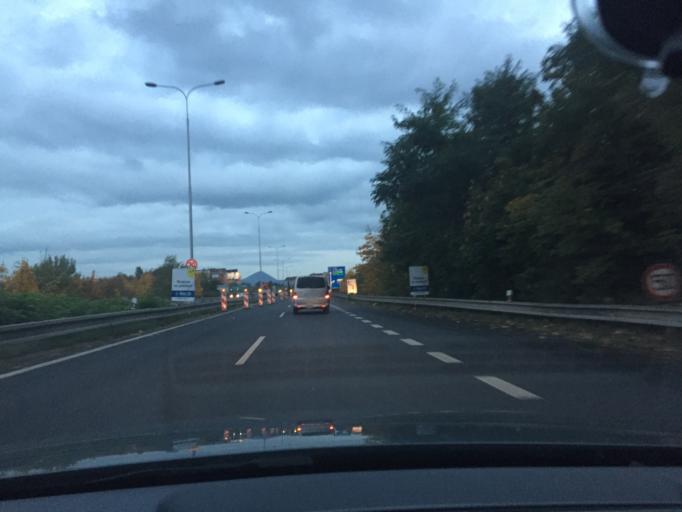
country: CZ
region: Ustecky
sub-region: Okres Teplice
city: Teplice
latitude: 50.6455
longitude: 13.8174
